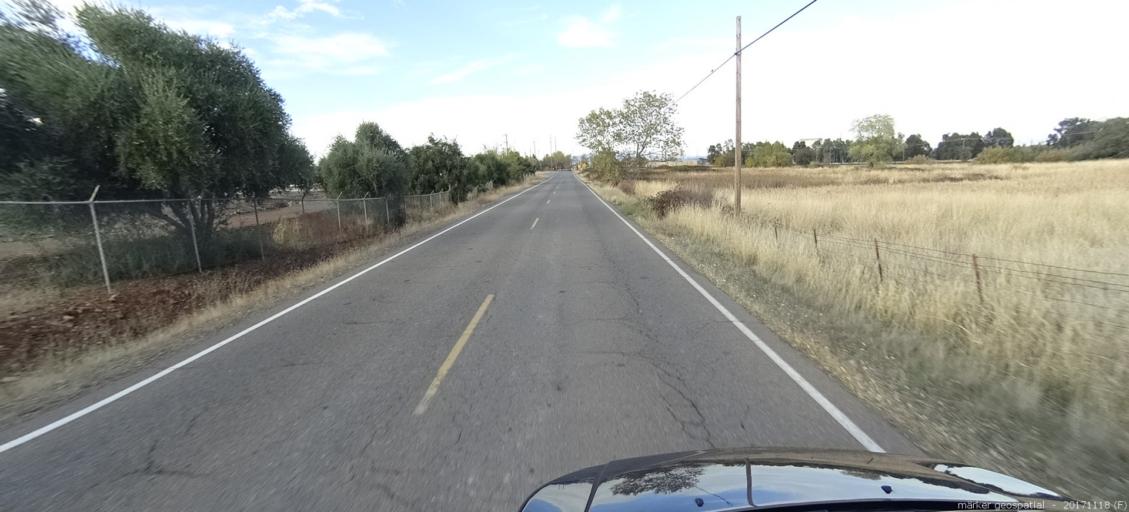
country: US
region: California
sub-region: Shasta County
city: Anderson
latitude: 40.4277
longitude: -122.2735
